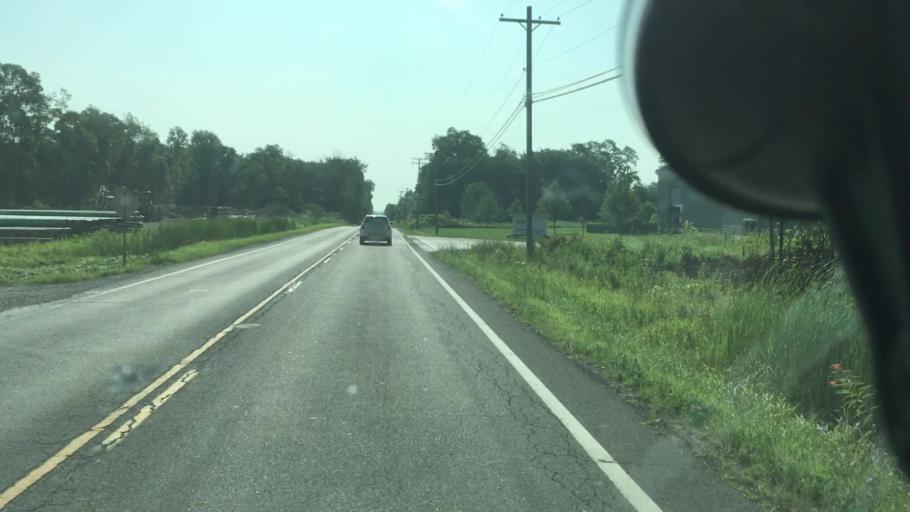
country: US
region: Ohio
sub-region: Mahoning County
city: Lowellville
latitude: 41.0239
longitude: -80.5468
